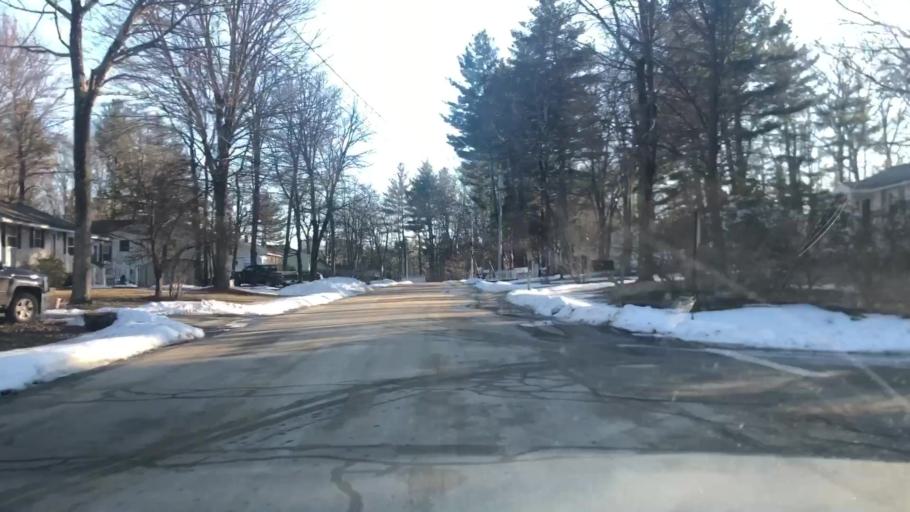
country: US
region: New Hampshire
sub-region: Hillsborough County
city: Milford
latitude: 42.8350
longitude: -71.6723
